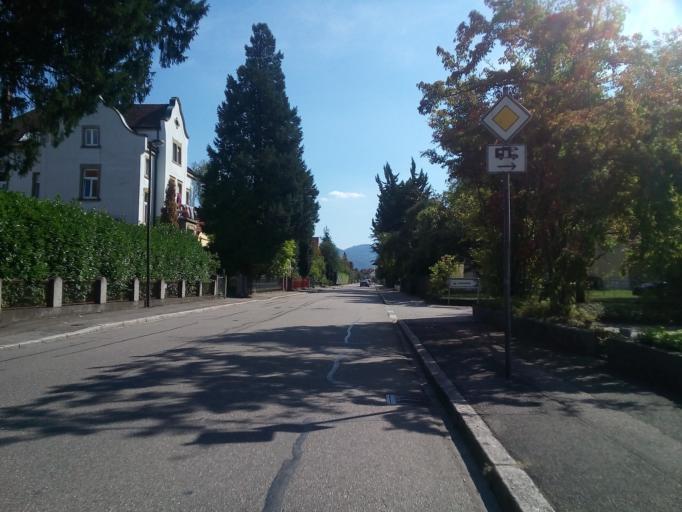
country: DE
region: Baden-Wuerttemberg
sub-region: Freiburg Region
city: Achern
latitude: 48.6254
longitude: 8.0762
